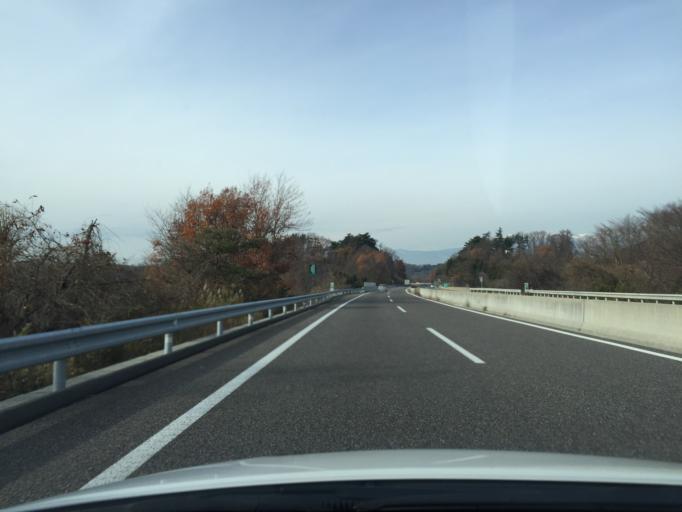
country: JP
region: Fukushima
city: Miharu
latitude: 37.4305
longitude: 140.4780
